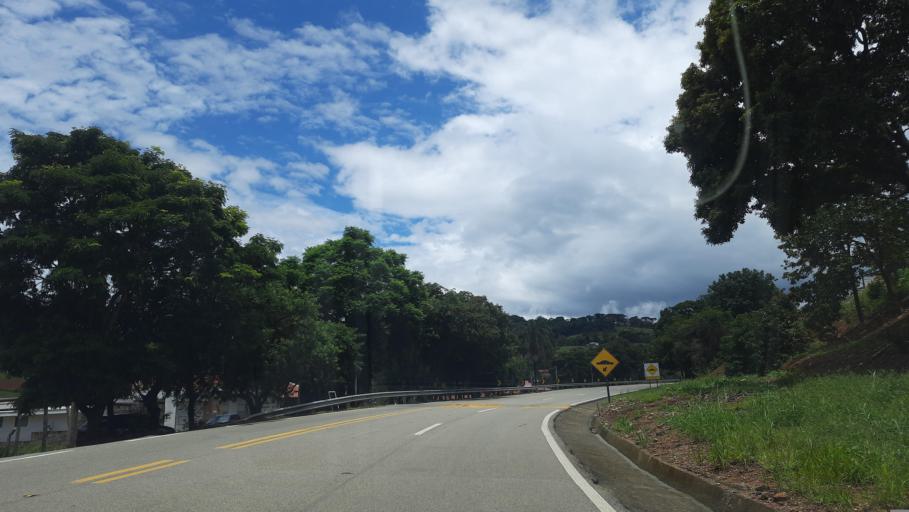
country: BR
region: Sao Paulo
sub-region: Sao Joao Da Boa Vista
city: Sao Joao da Boa Vista
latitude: -21.8352
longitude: -46.7445
